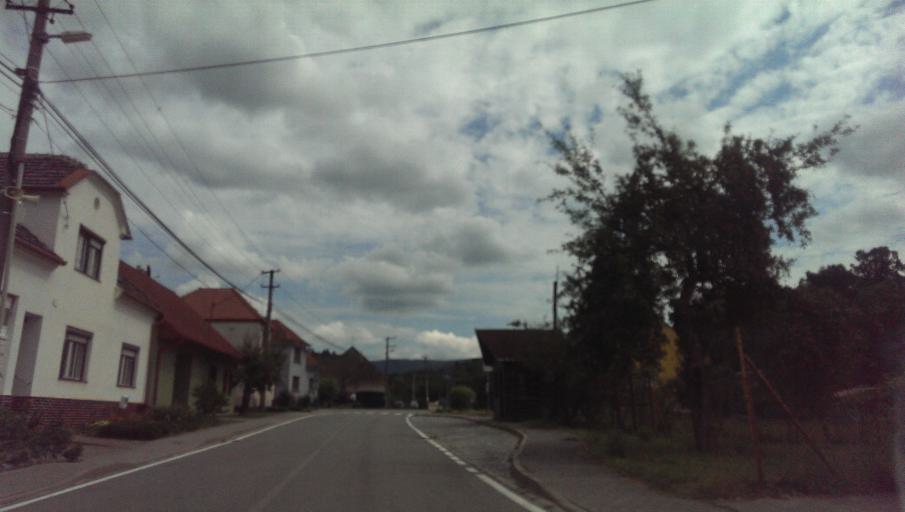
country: CZ
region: South Moravian
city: Velka nad Velickou
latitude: 48.8843
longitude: 17.5781
